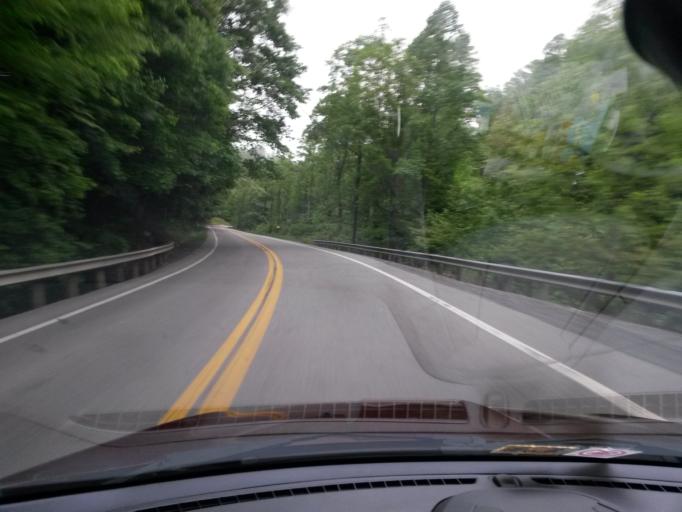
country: US
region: West Virginia
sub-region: Wyoming County
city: Pineville
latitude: 37.5526
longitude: -81.5690
